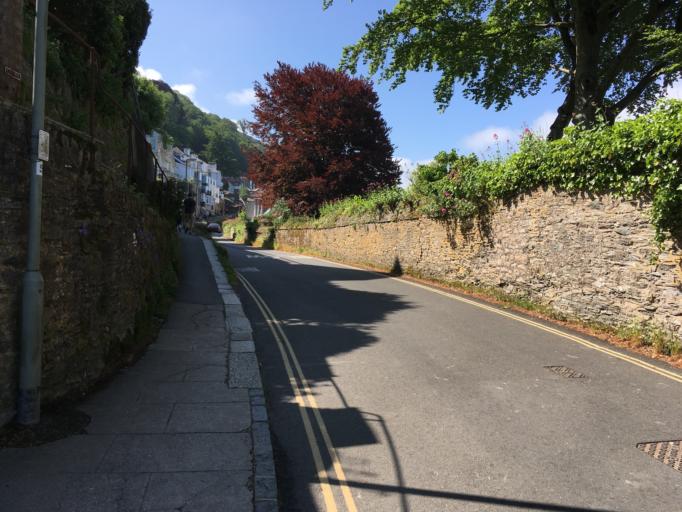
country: GB
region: England
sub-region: Devon
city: Dartmouth
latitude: 50.3437
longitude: -3.5737
